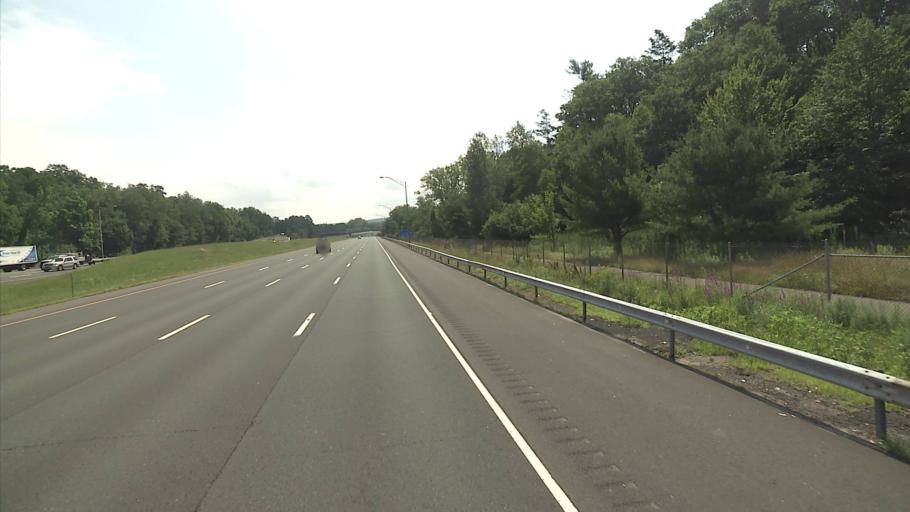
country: US
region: Connecticut
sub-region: Hartford County
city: Manchester
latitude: 41.7625
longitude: -72.5269
